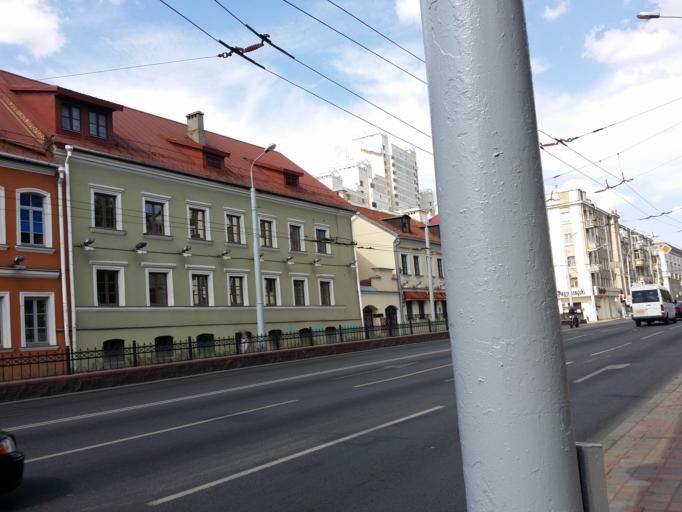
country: BY
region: Minsk
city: Minsk
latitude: 53.9085
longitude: 27.5575
